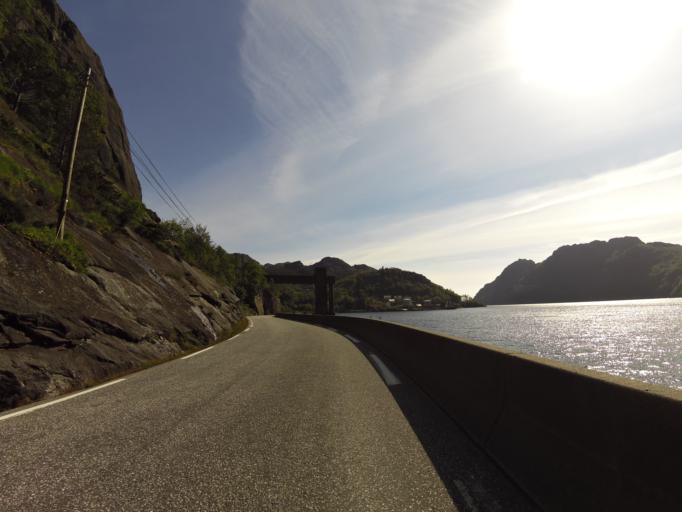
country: NO
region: Rogaland
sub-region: Sokndal
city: Hauge i Dalane
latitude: 58.3214
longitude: 6.3497
